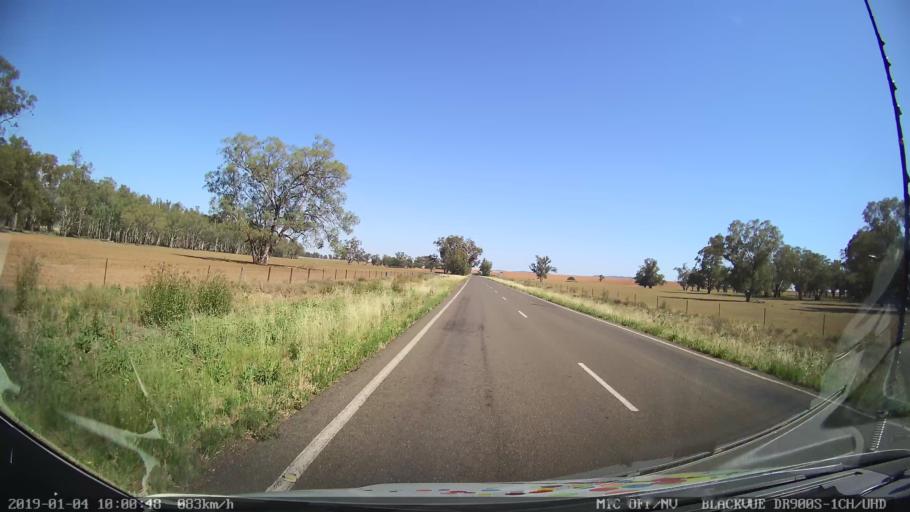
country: AU
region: New South Wales
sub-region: Cabonne
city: Canowindra
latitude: -33.4935
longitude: 148.3765
